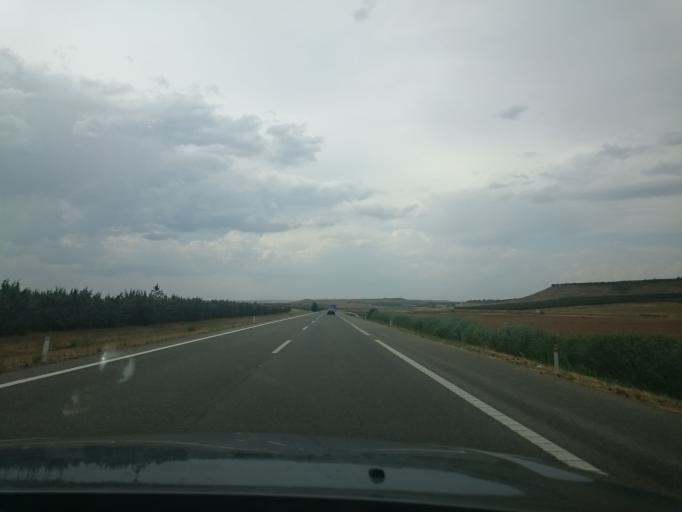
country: ES
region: Navarre
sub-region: Provincia de Navarra
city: Fontellas
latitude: 41.9987
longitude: -1.5820
